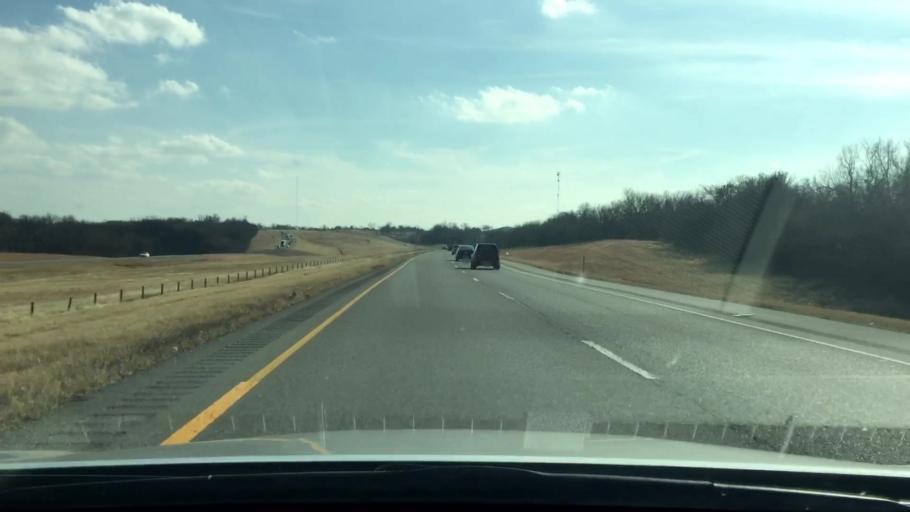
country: US
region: Oklahoma
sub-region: McClain County
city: Purcell
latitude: 34.9567
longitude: -97.3692
